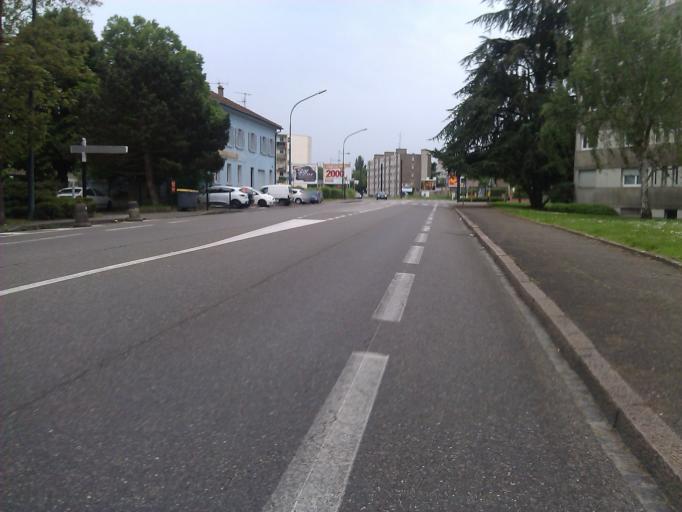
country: FR
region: Alsace
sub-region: Departement du Haut-Rhin
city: Kingersheim
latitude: 47.7793
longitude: 7.3290
